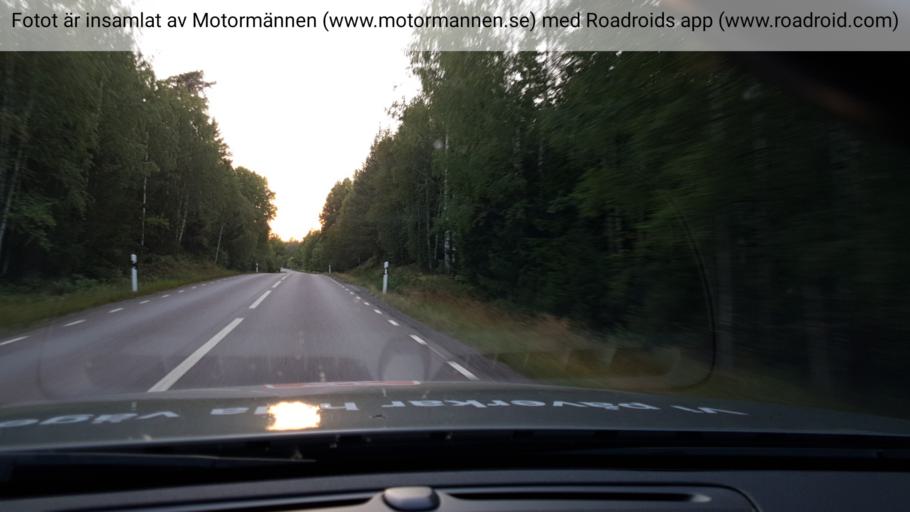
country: SE
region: Uppsala
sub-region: Heby Kommun
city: OEstervala
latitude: 60.0319
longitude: 17.2731
